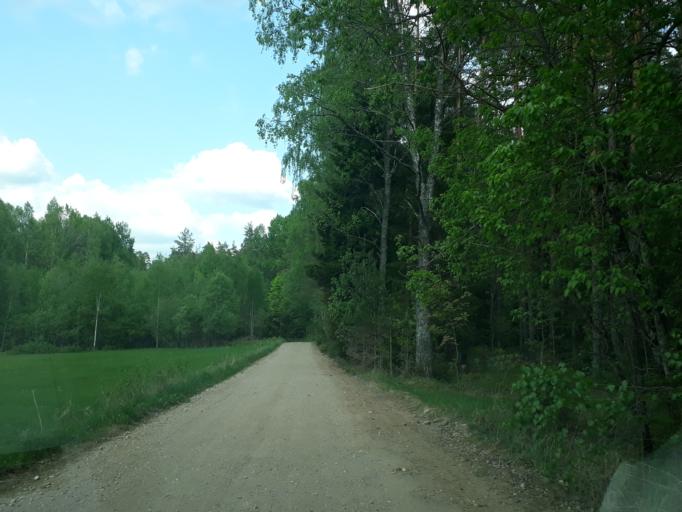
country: LV
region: Ligatne
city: Ligatne
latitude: 57.2739
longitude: 24.9888
